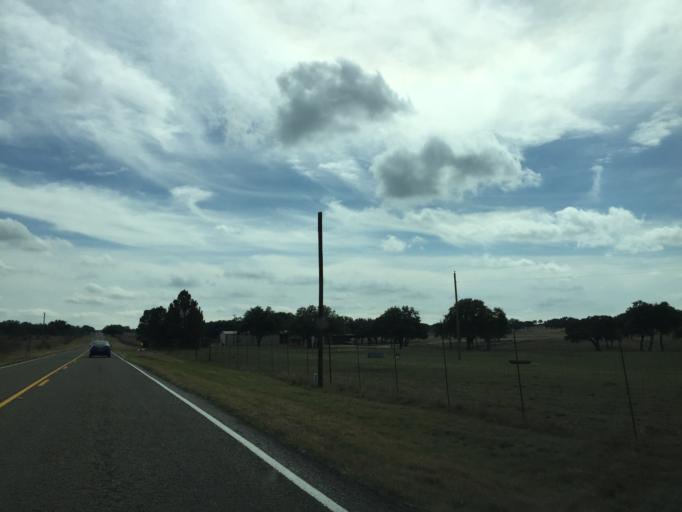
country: US
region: Texas
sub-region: Burnet County
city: Granite Shoals
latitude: 30.5215
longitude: -98.4469
